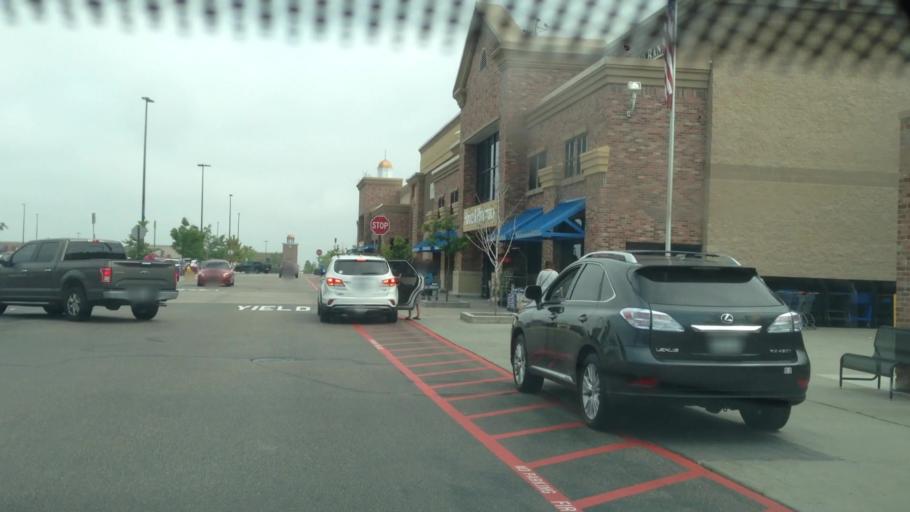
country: US
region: Colorado
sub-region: Douglas County
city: Parker
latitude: 39.6057
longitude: -104.7055
